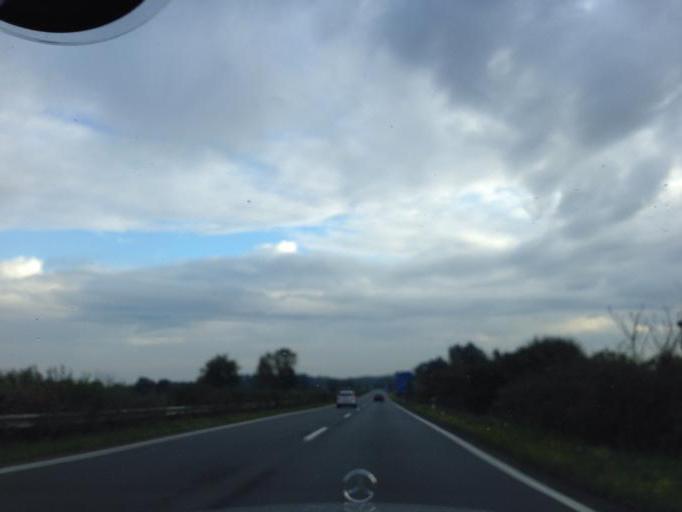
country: DE
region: Schleswig-Holstein
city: Grabau
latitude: 53.8060
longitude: 10.3193
